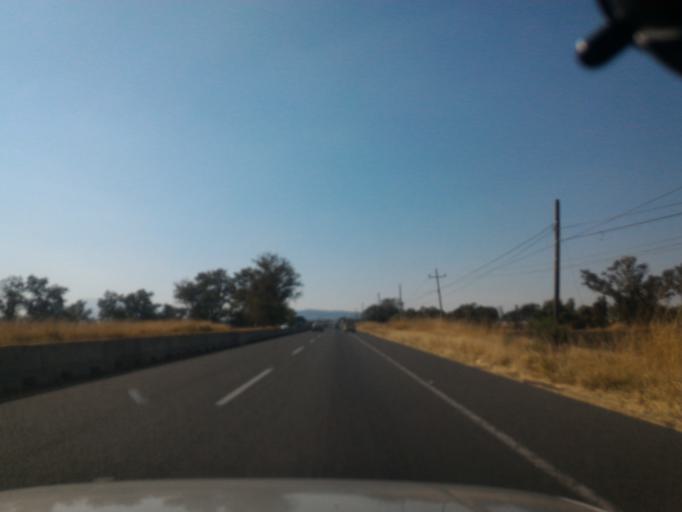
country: MX
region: Jalisco
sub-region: Ixtlahuacan de los Membrillos
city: Valle de los Girasoles [Fraccionamiento]
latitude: 20.4036
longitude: -103.1753
